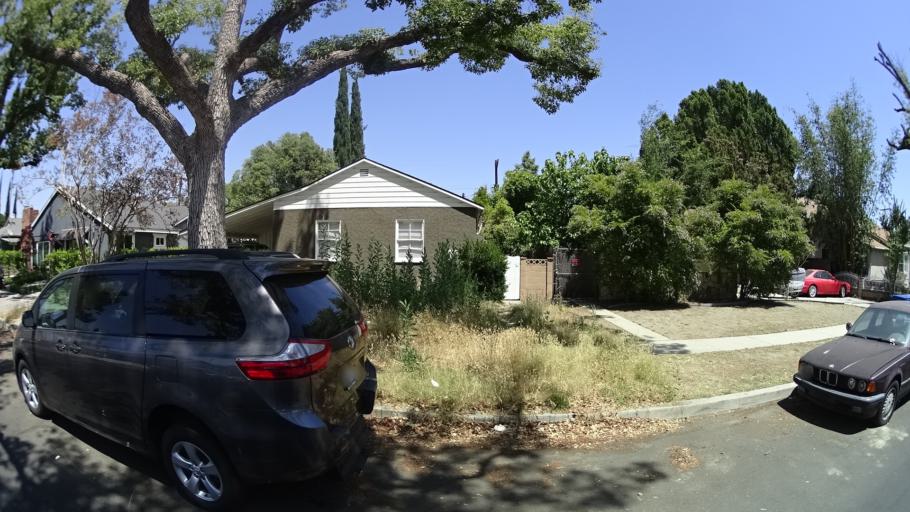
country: US
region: California
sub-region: Los Angeles County
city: Van Nuys
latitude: 34.2141
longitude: -118.4390
